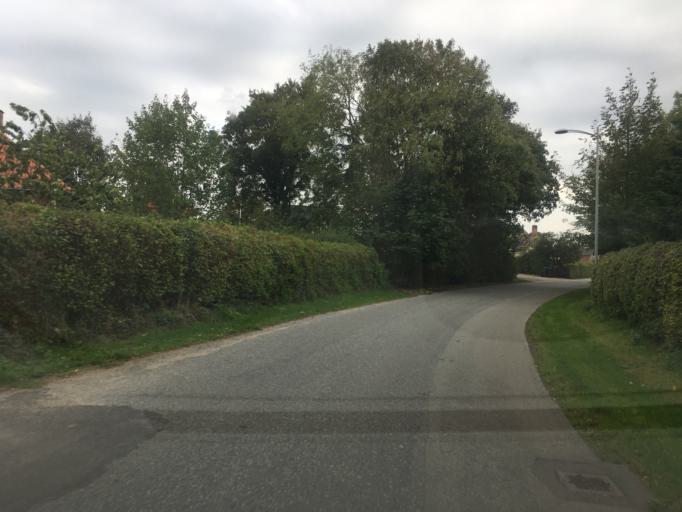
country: DK
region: South Denmark
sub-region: Tonder Kommune
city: Logumkloster
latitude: 55.0051
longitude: 9.0376
